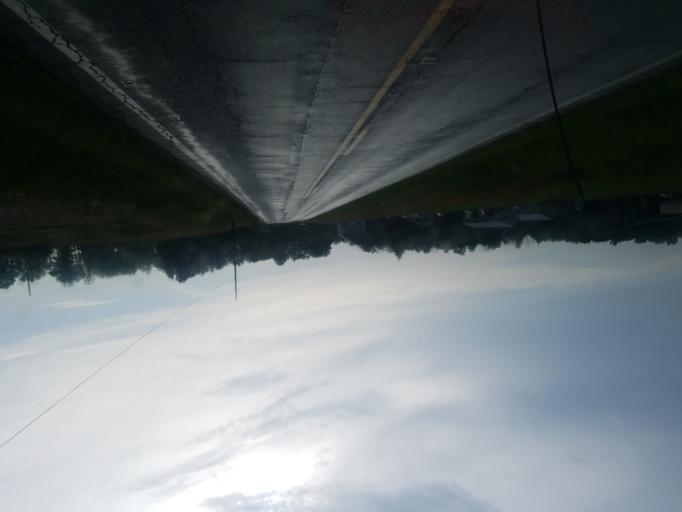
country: US
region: Ohio
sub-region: Medina County
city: Lodi
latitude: 40.9451
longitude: -81.9916
